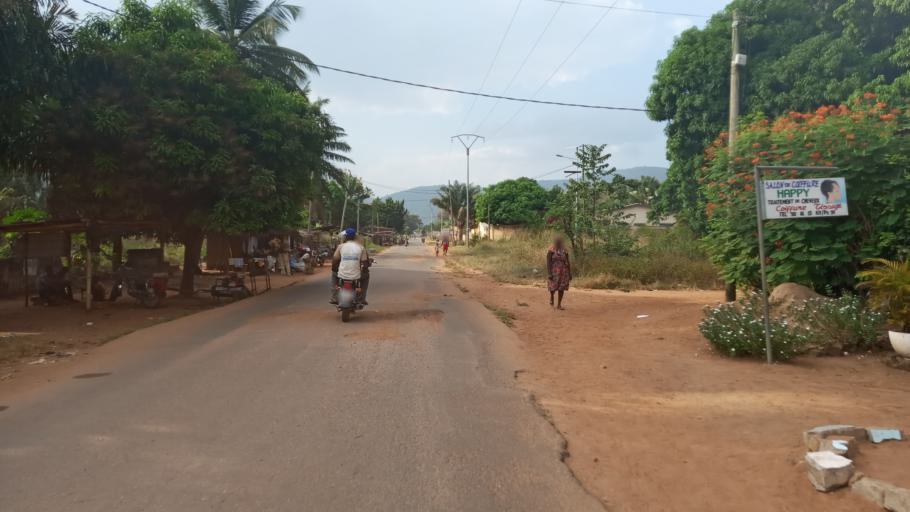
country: TG
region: Plateaux
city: Kpalime
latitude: 6.9216
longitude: 0.6195
